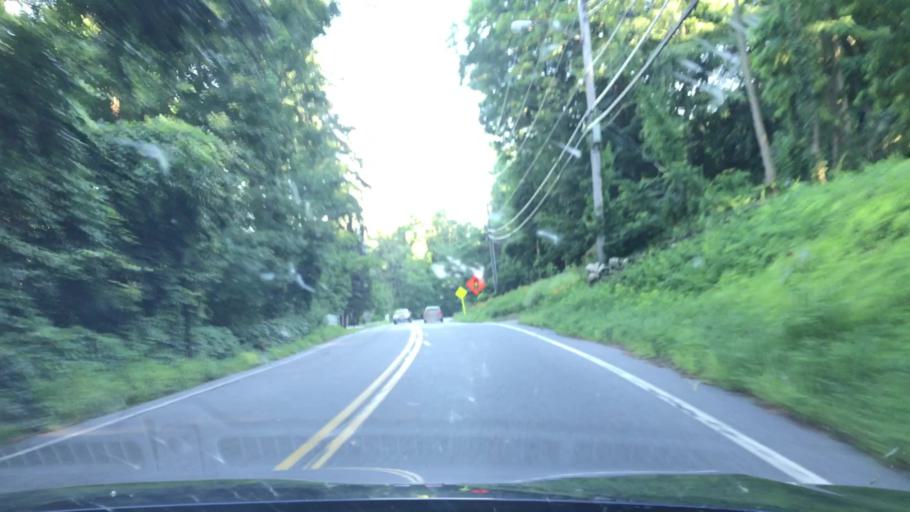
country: US
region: New York
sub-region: Westchester County
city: Heritage Hills
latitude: 41.3595
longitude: -73.6735
